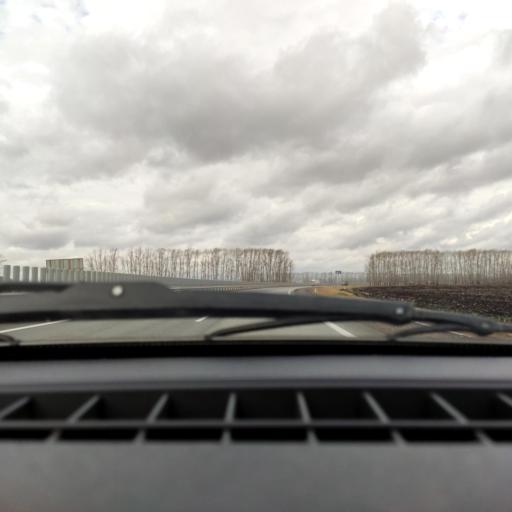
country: RU
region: Bashkortostan
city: Asanovo
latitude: 54.9232
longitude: 55.5784
